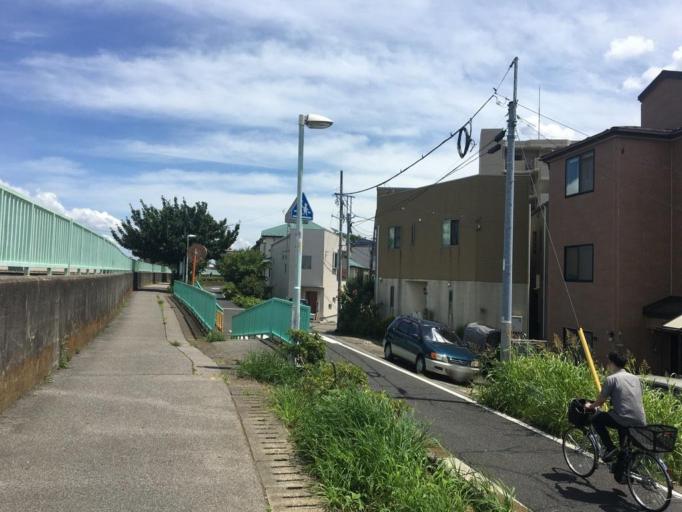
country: JP
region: Chiba
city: Matsudo
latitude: 35.7417
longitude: 139.8582
